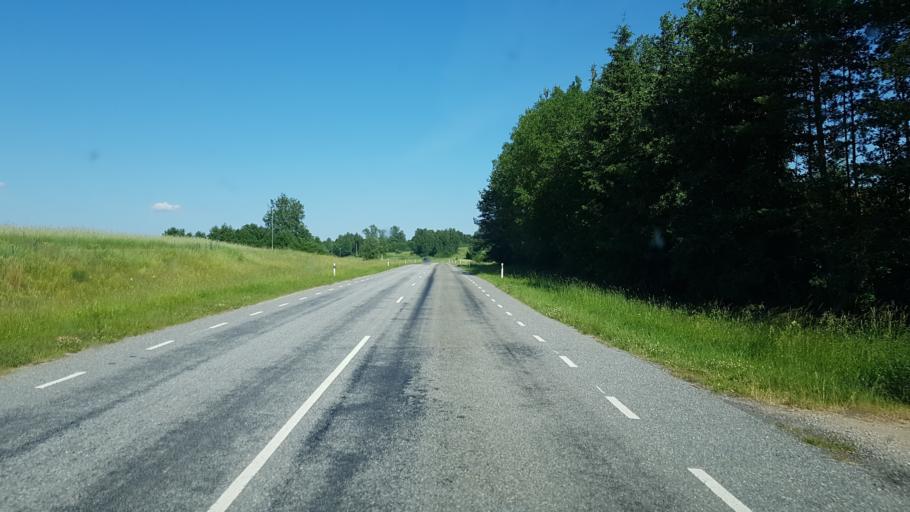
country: EE
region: Vorumaa
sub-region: Voru linn
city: Voru
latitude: 57.8577
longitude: 27.1180
